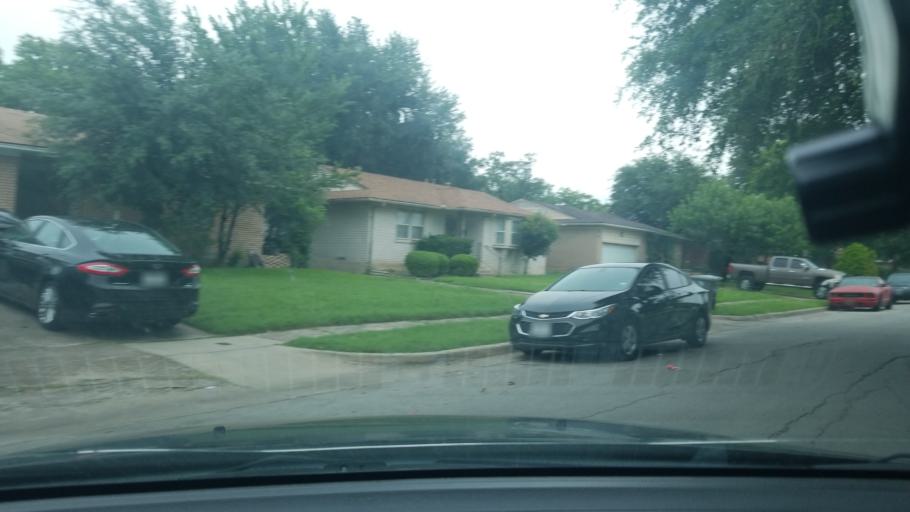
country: US
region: Texas
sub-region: Dallas County
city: Balch Springs
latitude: 32.7537
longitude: -96.6751
